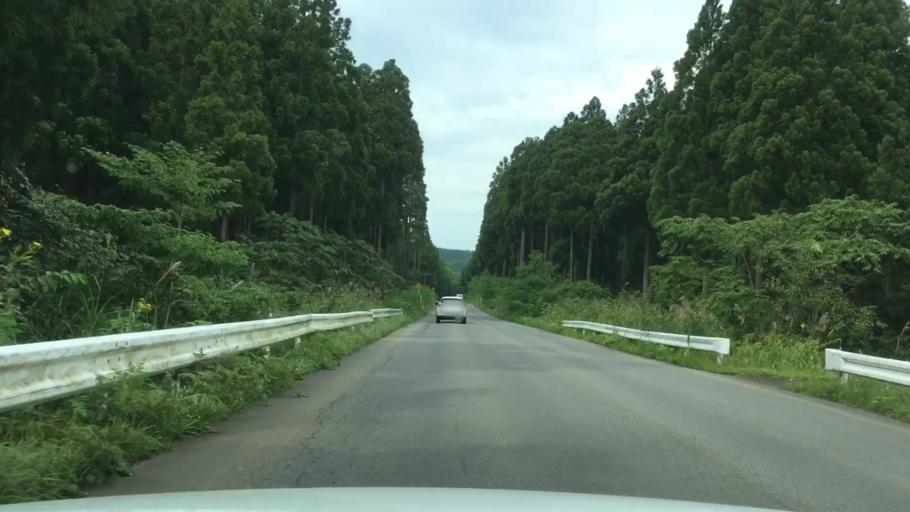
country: JP
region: Aomori
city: Shimokizukuri
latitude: 40.7108
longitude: 140.2716
